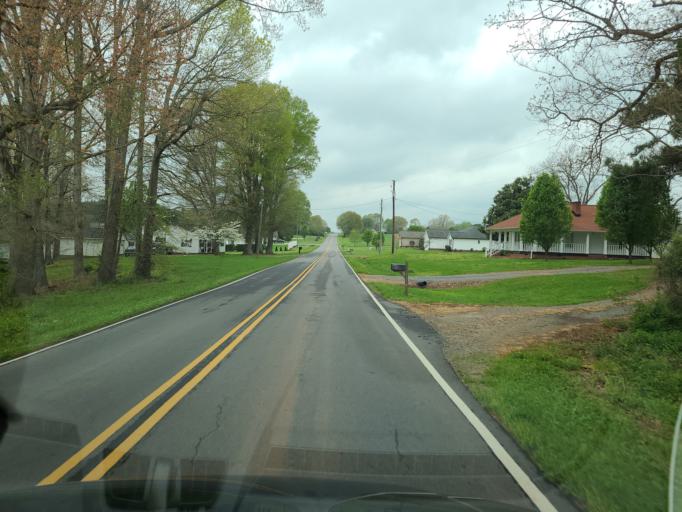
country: US
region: North Carolina
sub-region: Lincoln County
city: Lincolnton
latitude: 35.4606
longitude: -81.3208
